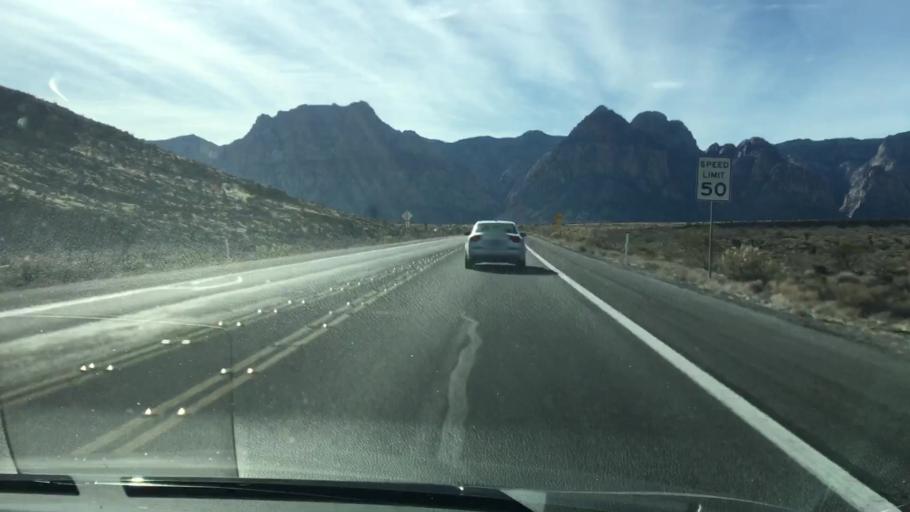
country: US
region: Nevada
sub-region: Clark County
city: Summerlin South
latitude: 36.1295
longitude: -115.4254
